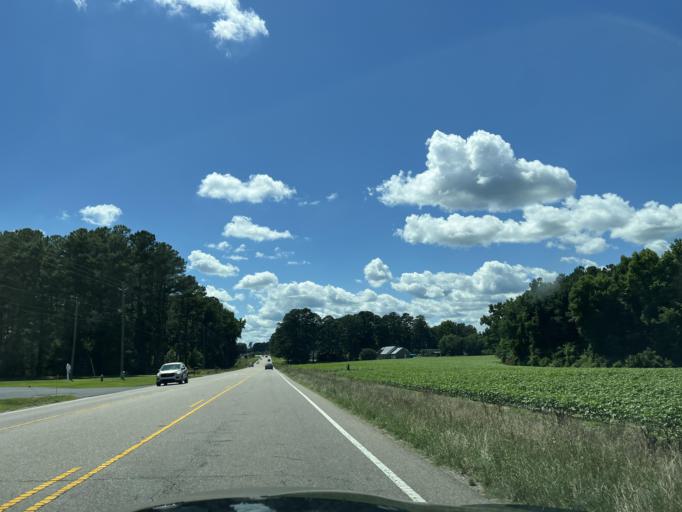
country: US
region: North Carolina
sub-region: Lee County
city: Sanford
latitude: 35.4379
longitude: -79.2032
